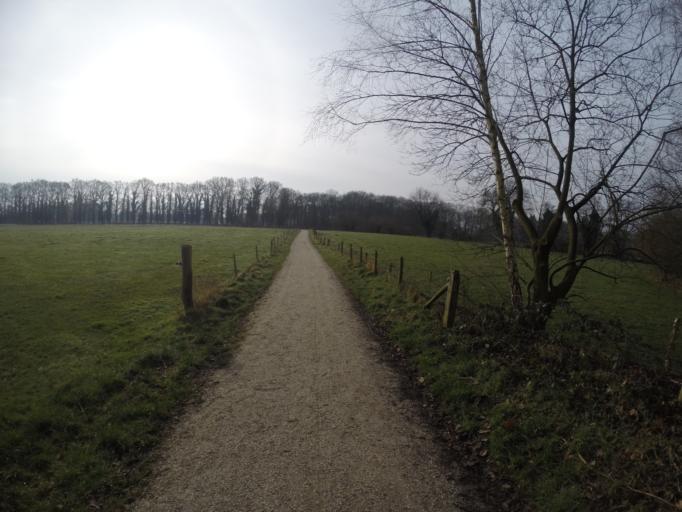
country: NL
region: Gelderland
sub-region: Gemeente Bronckhorst
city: Hengelo
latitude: 52.1012
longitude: 6.3022
